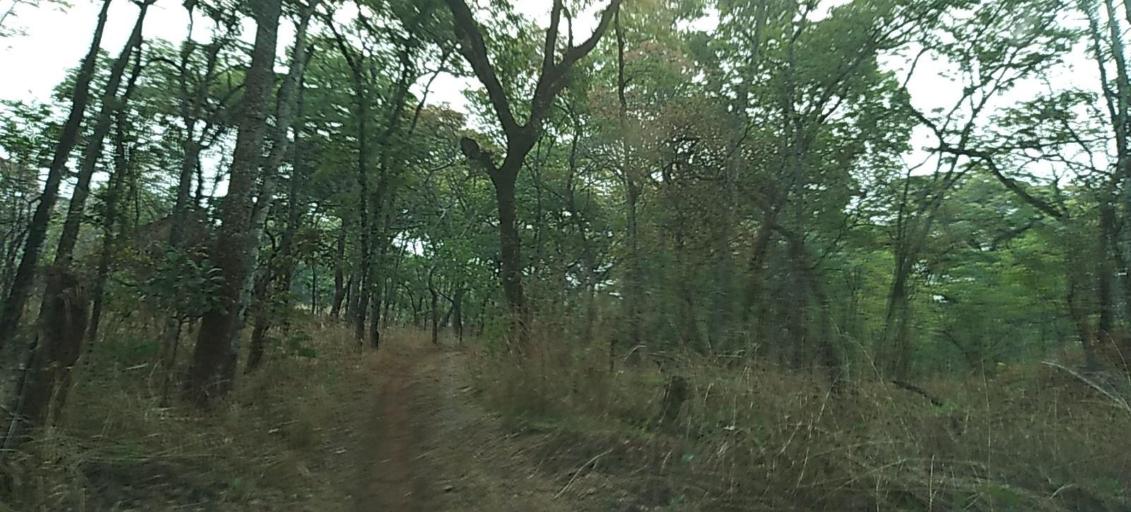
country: ZM
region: North-Western
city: Solwezi
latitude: -12.0451
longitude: 26.0152
